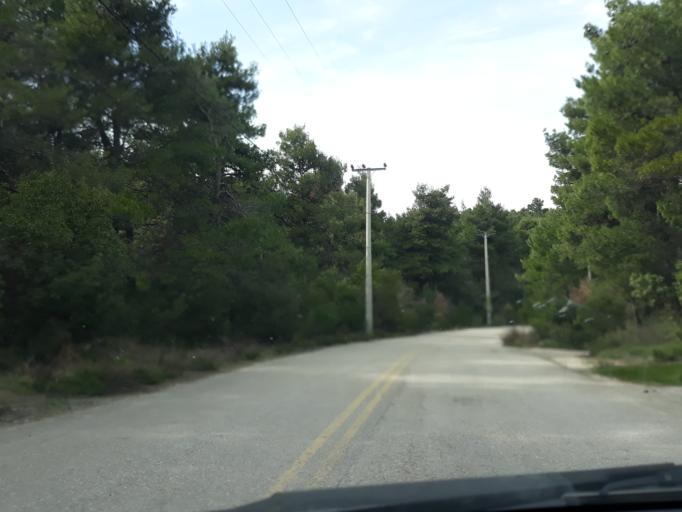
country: GR
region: Attica
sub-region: Nomarchia Anatolikis Attikis
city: Afidnes
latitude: 38.1979
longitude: 23.7917
